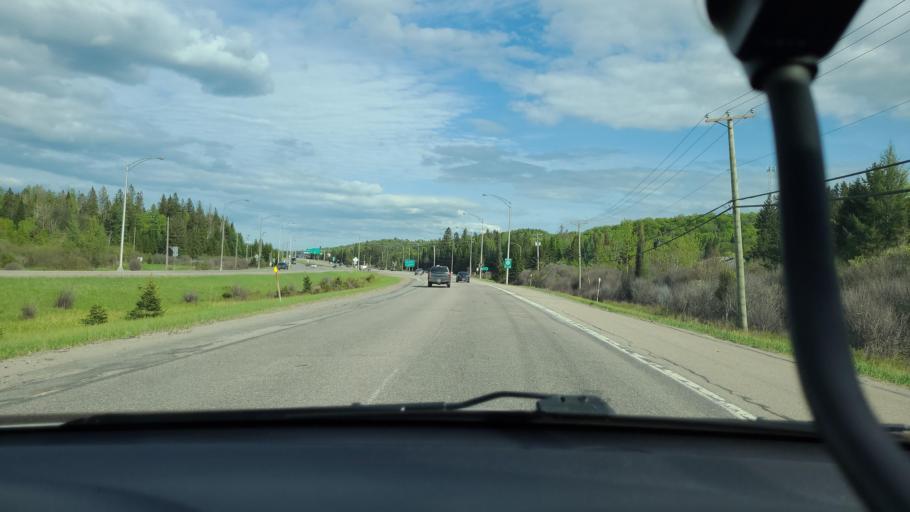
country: CA
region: Quebec
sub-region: Laurentides
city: Sainte-Agathe-des-Monts
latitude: 46.0666
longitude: -74.3106
